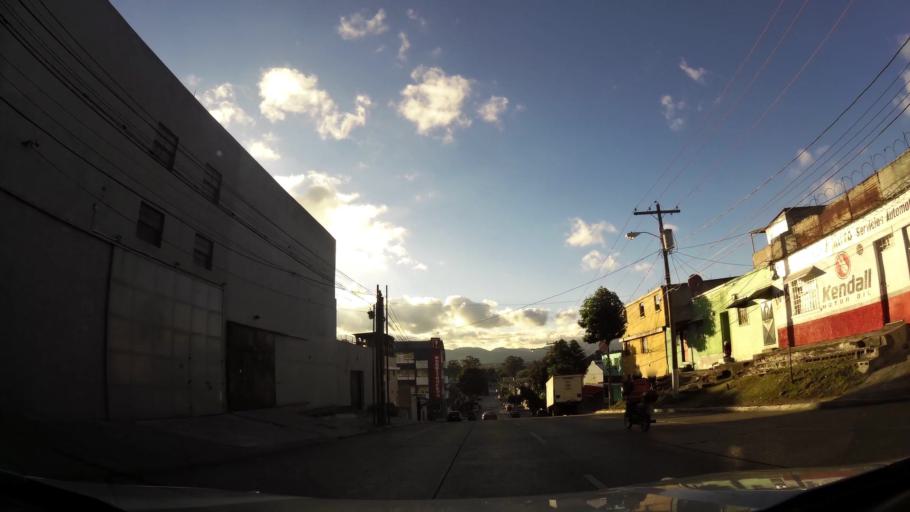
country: GT
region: Guatemala
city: Guatemala City
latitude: 14.6268
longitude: -90.5239
